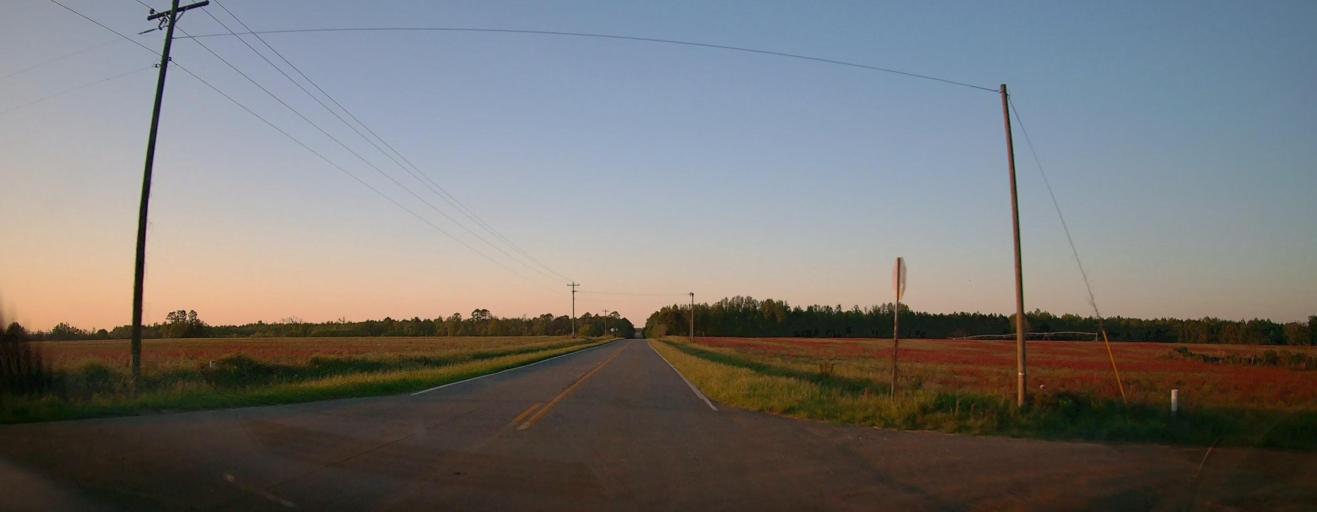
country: US
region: Georgia
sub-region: Ben Hill County
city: Fitzgerald
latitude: 31.7309
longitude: -83.3098
